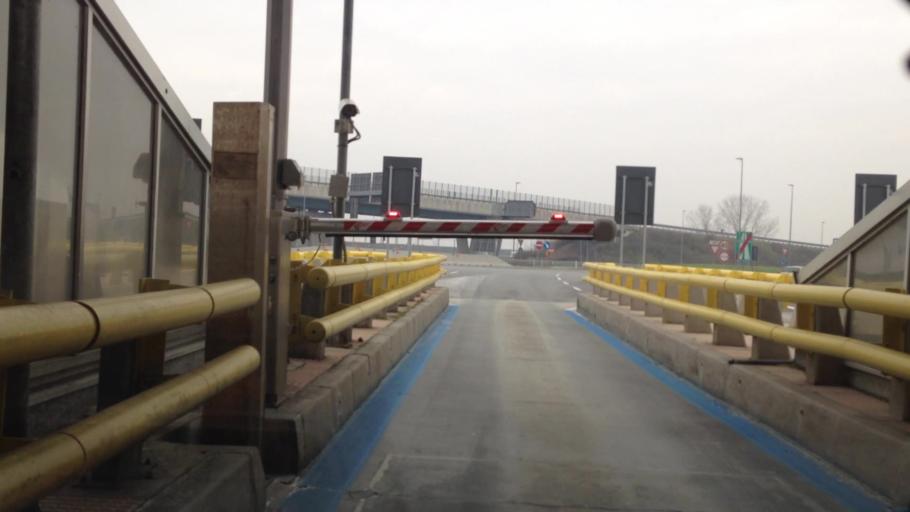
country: IT
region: Piedmont
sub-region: Provincia di Vercelli
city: Borgo d'Ale
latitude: 45.3219
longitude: 8.0717
